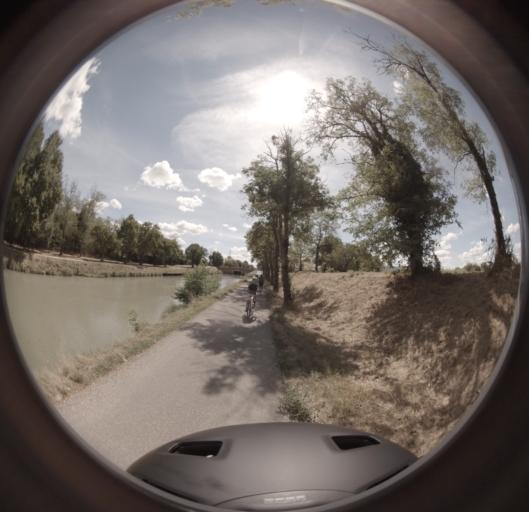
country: FR
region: Midi-Pyrenees
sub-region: Departement du Tarn-et-Garonne
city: Moissac
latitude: 44.0683
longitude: 1.1007
